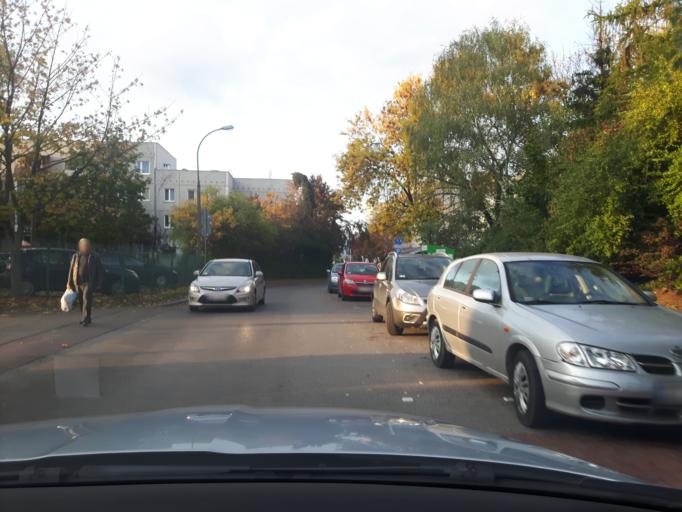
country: PL
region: Masovian Voivodeship
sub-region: Warszawa
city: Ursynow
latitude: 52.1542
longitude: 21.0198
